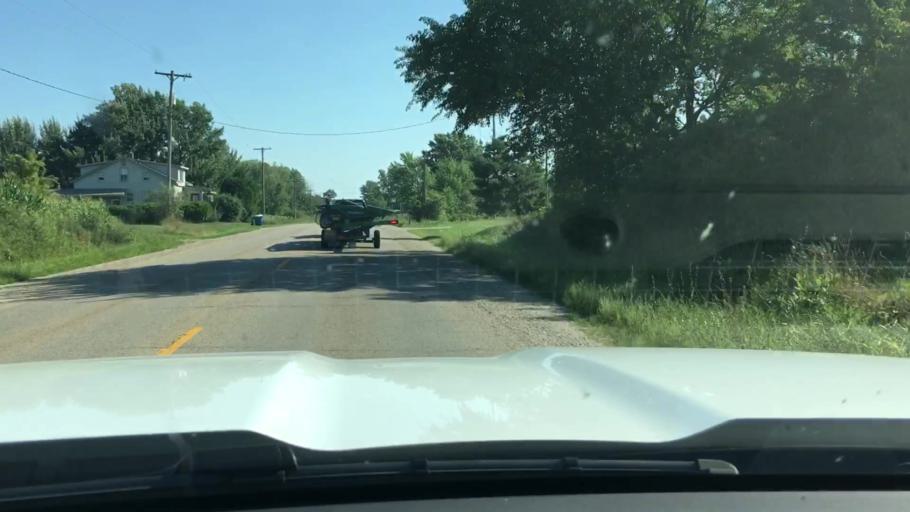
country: US
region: Michigan
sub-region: Ottawa County
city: Coopersville
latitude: 43.0711
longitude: -85.9569
